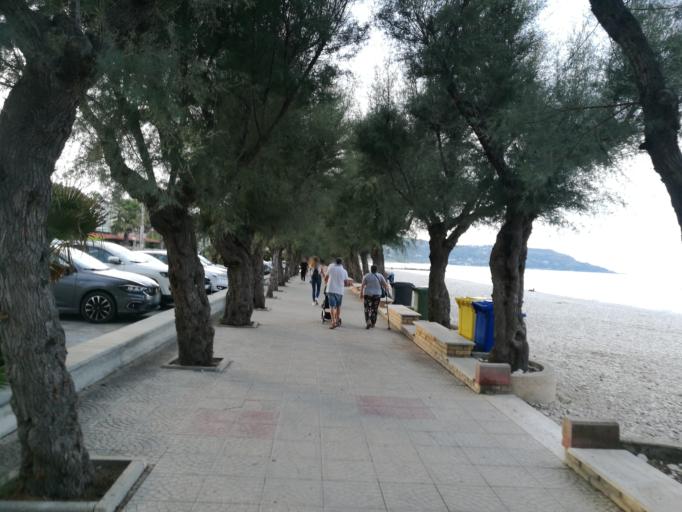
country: IT
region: Abruzzo
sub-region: Provincia di Chieti
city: Fossacesia
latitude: 42.2470
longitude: 14.5166
